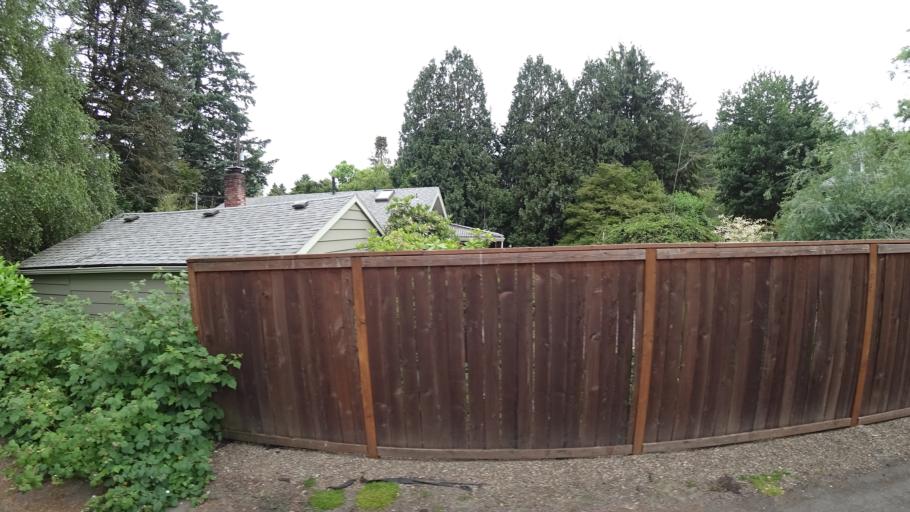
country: US
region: Oregon
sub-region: Multnomah County
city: Lents
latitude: 45.5088
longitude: -122.5863
